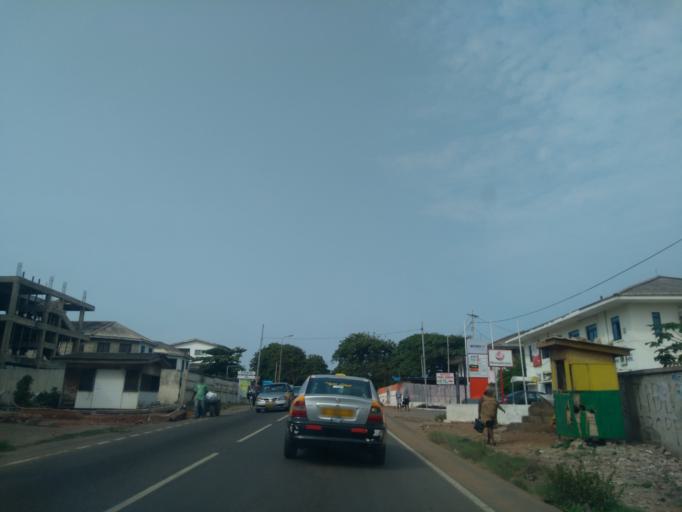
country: GH
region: Greater Accra
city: Accra
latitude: 5.5513
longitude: -0.1805
